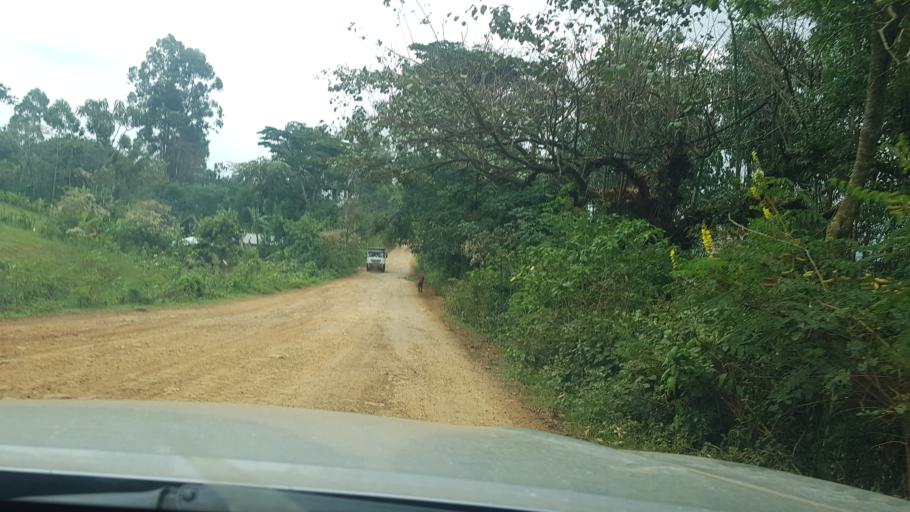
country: ET
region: Oromiya
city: Gore
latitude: 7.8302
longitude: 35.4666
